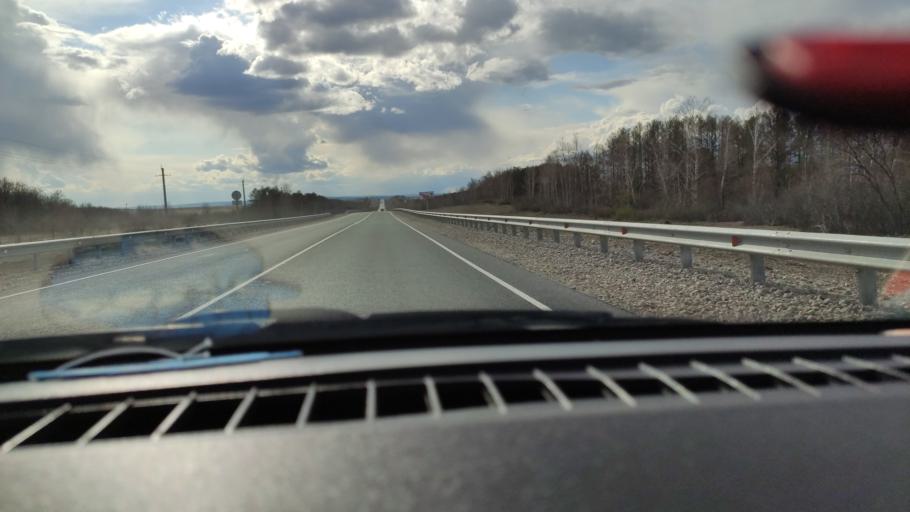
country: RU
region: Saratov
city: Shikhany
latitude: 52.1614
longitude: 47.1480
